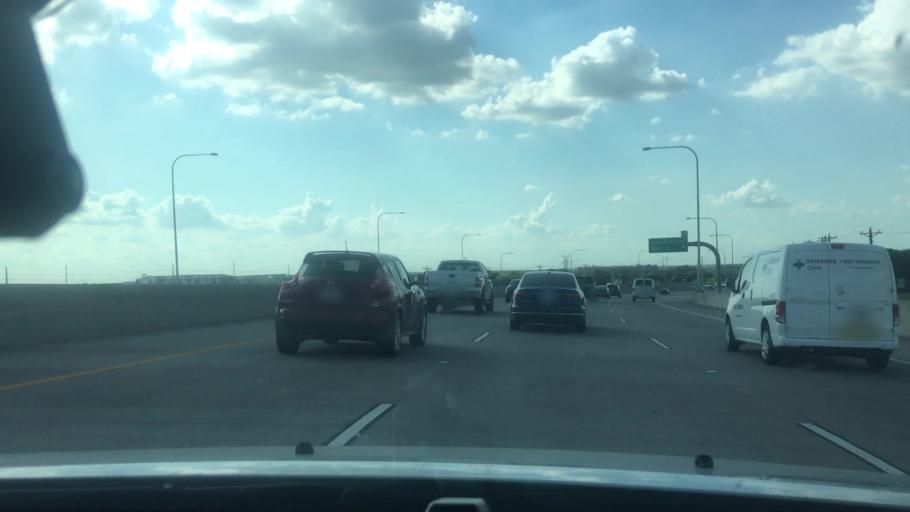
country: US
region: Texas
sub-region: Collin County
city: Frisco
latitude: 33.1383
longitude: -96.8365
